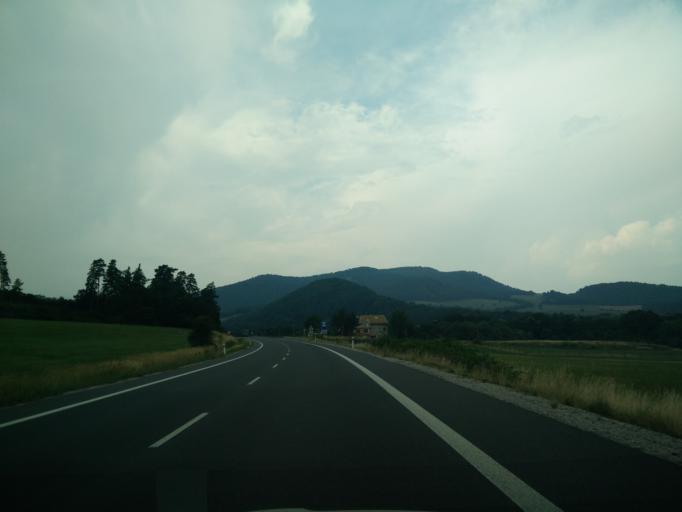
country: SK
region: Nitriansky
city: Handlova
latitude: 48.6430
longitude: 18.7696
